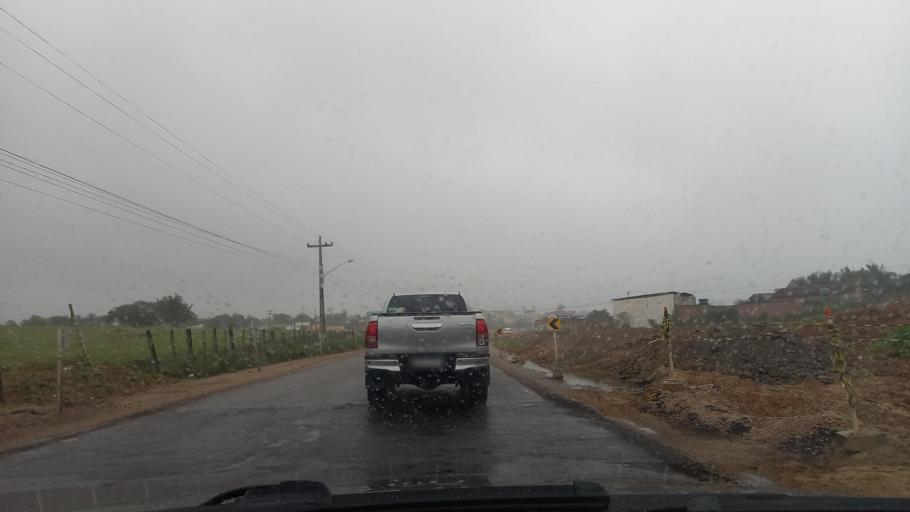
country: BR
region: Alagoas
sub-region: Arapiraca
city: Arapiraca
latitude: -9.7126
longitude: -36.7146
